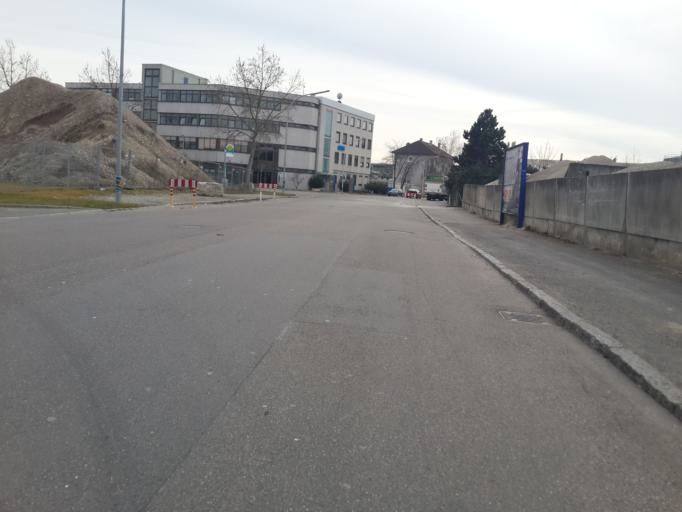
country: DE
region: Baden-Wuerttemberg
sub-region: Regierungsbezirk Stuttgart
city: Heilbronn
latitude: 49.1561
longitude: 9.2144
